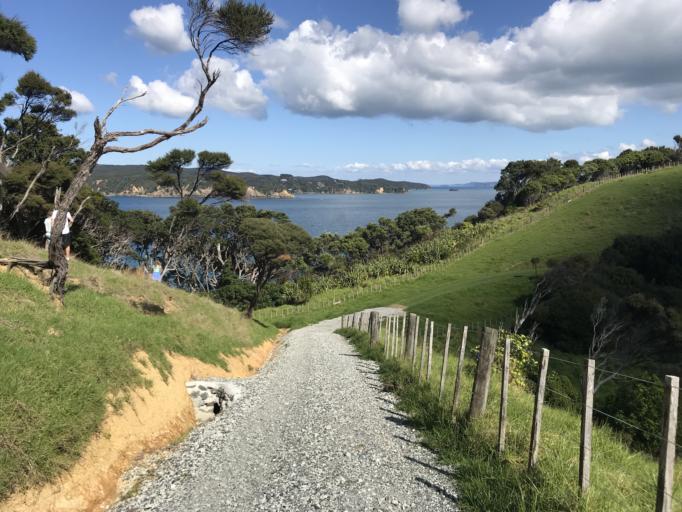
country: NZ
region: Auckland
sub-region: Auckland
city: Warkworth
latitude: -36.3771
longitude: 174.8429
